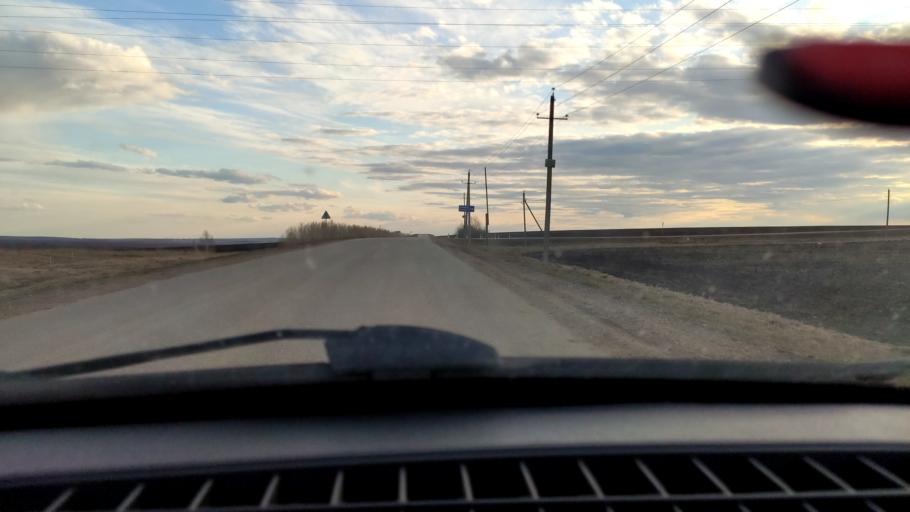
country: RU
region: Bashkortostan
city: Tolbazy
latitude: 53.9861
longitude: 55.8003
